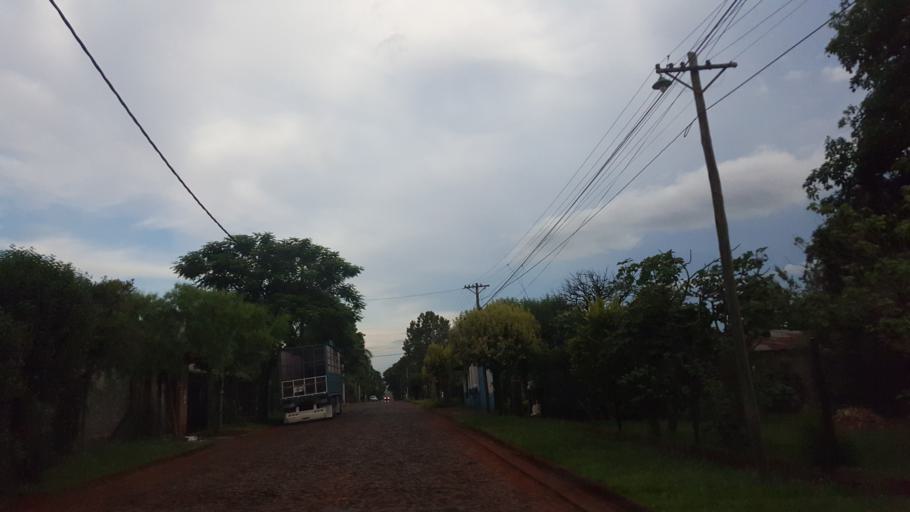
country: AR
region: Misiones
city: Jardin America
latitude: -27.0487
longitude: -55.2425
